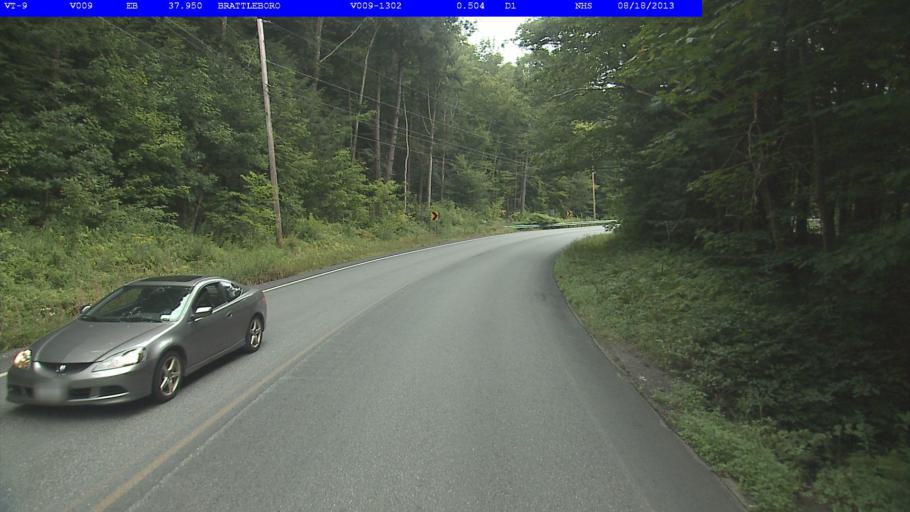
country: US
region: Vermont
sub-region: Windham County
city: West Brattleboro
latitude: 42.8770
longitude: -72.6696
